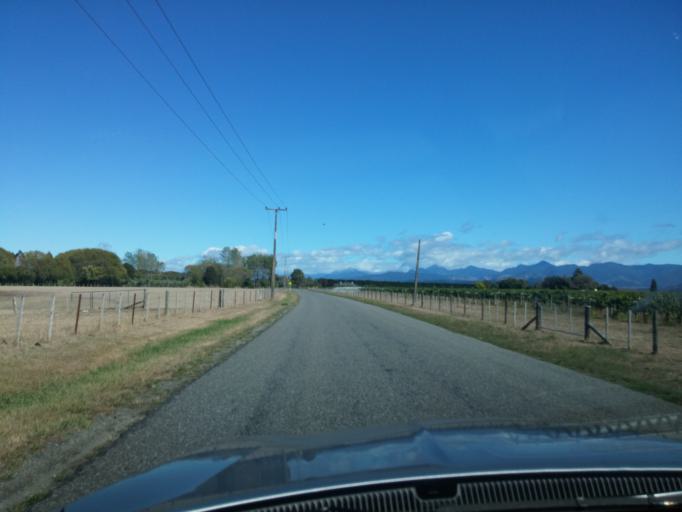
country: NZ
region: Marlborough
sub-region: Marlborough District
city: Blenheim
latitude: -41.5264
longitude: 173.8435
